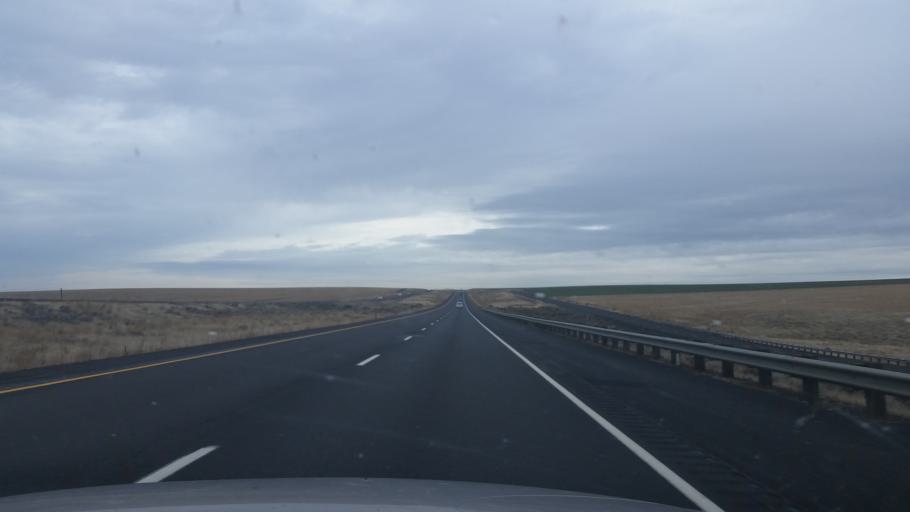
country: US
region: Washington
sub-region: Grant County
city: Warden
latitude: 47.0864
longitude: -118.7527
